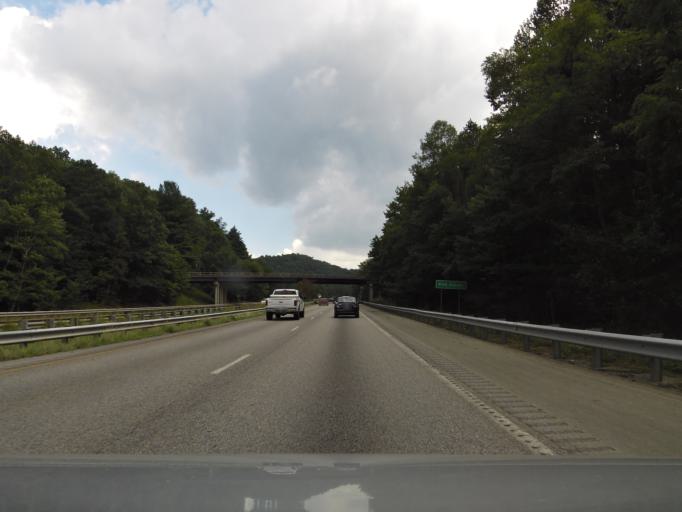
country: US
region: North Carolina
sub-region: Henderson County
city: East Flat Rock
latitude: 35.2547
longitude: -82.3496
